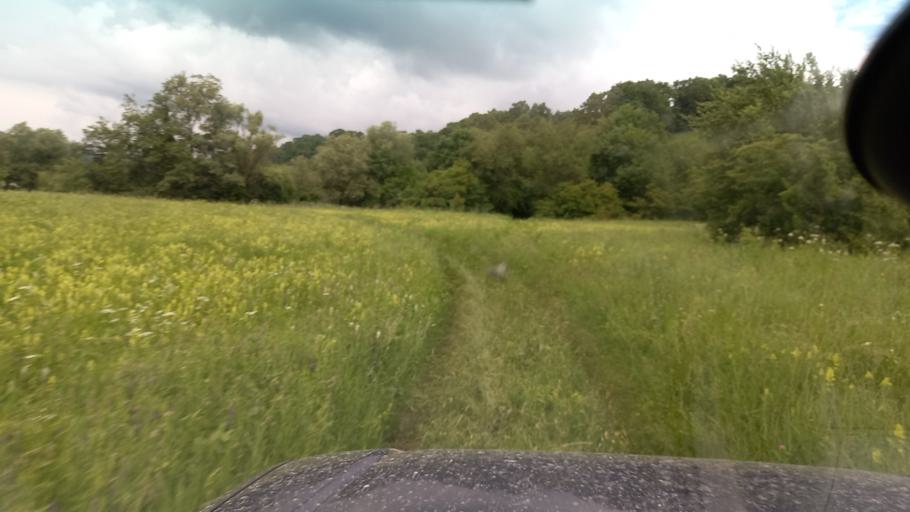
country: RU
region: Krasnodarskiy
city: Psebay
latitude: 44.1538
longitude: 40.8562
